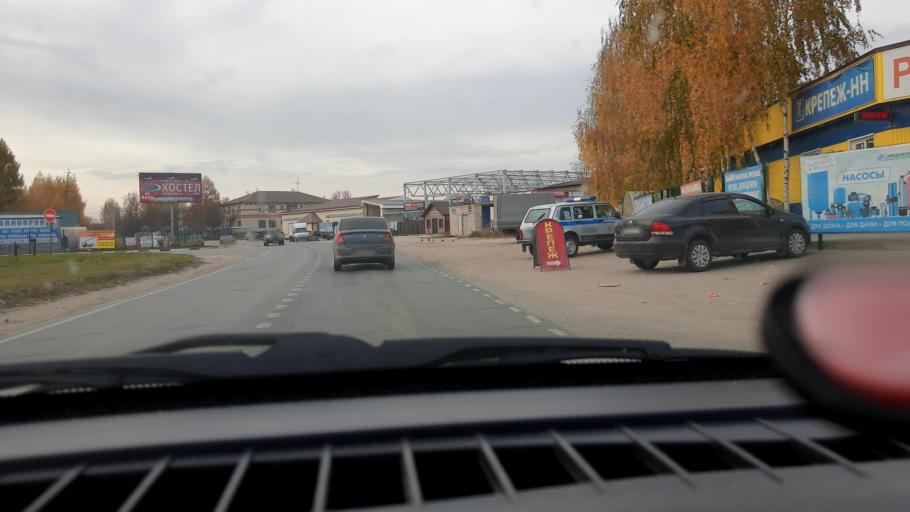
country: RU
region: Nizjnij Novgorod
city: Gorodets
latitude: 56.6407
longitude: 43.5007
